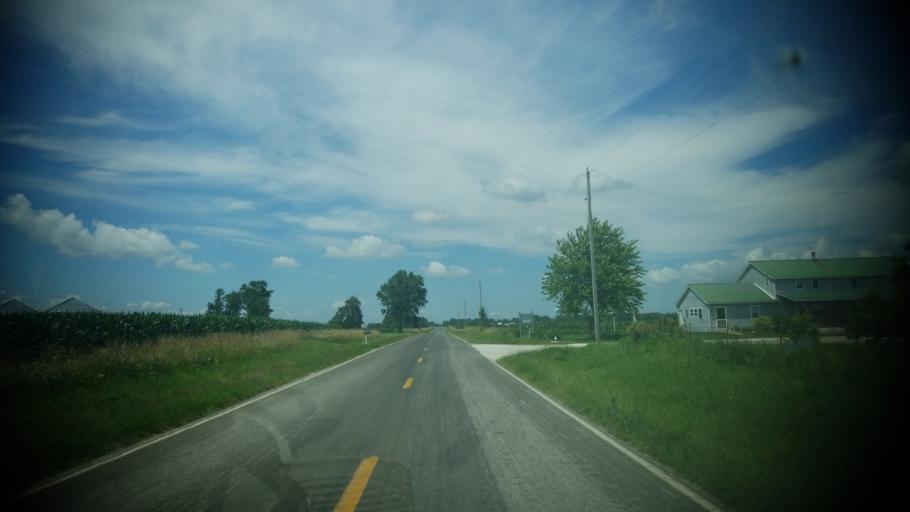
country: US
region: Missouri
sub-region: Audrain County
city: Vandalia
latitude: 39.3282
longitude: -91.3451
